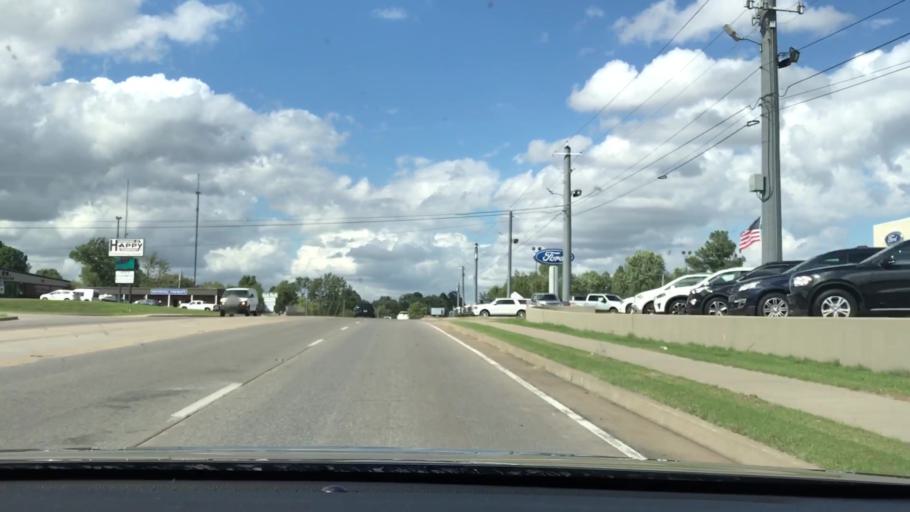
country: US
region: Kentucky
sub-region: Graves County
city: Mayfield
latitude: 36.7600
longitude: -88.6418
